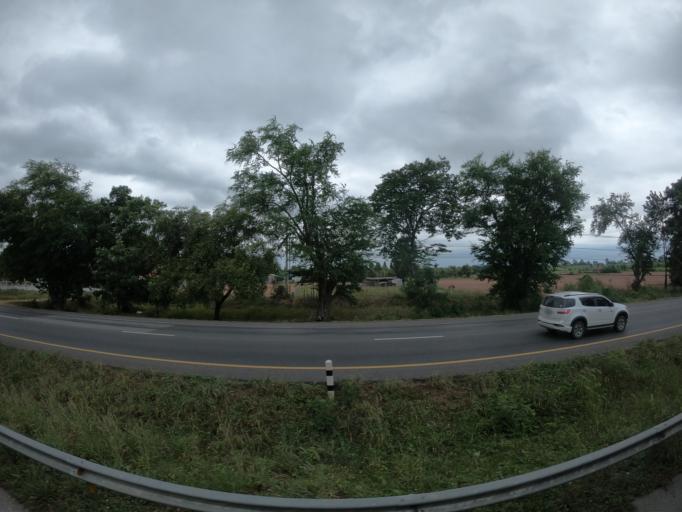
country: TH
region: Khon Kaen
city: Non Sila
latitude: 15.8958
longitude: 102.6486
